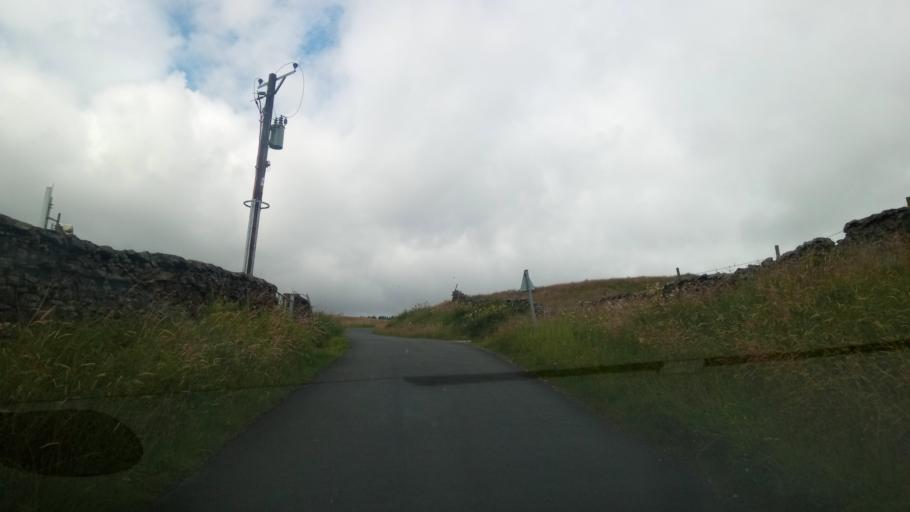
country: GB
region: England
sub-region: North Yorkshire
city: Ingleton
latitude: 54.2799
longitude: -2.3681
